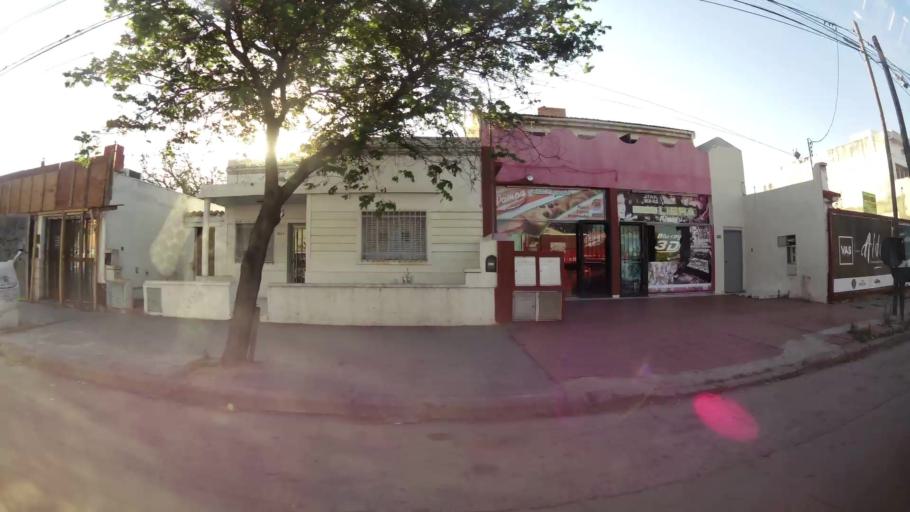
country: AR
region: Cordoba
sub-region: Departamento de Capital
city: Cordoba
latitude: -31.3748
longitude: -64.2065
